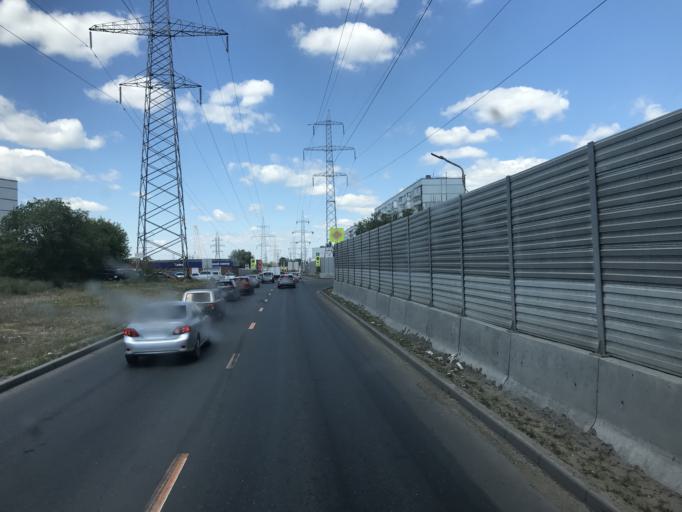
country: RU
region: Samara
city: Zhigulevsk
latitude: 53.4743
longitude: 49.5121
